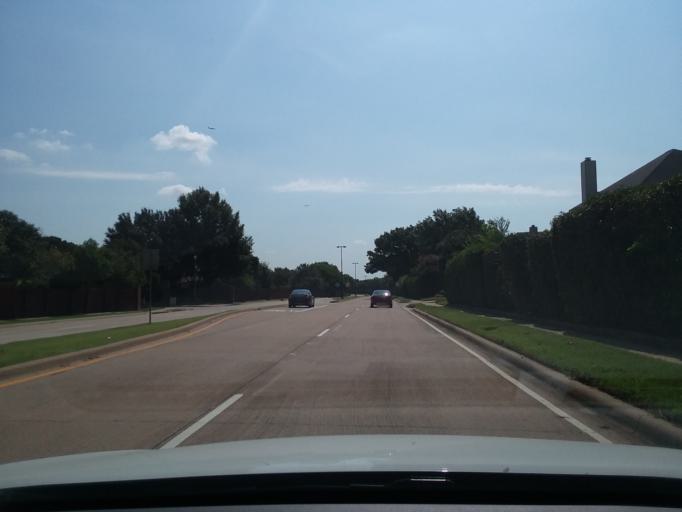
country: US
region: Texas
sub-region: Denton County
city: Flower Mound
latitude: 33.0198
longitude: -97.0517
